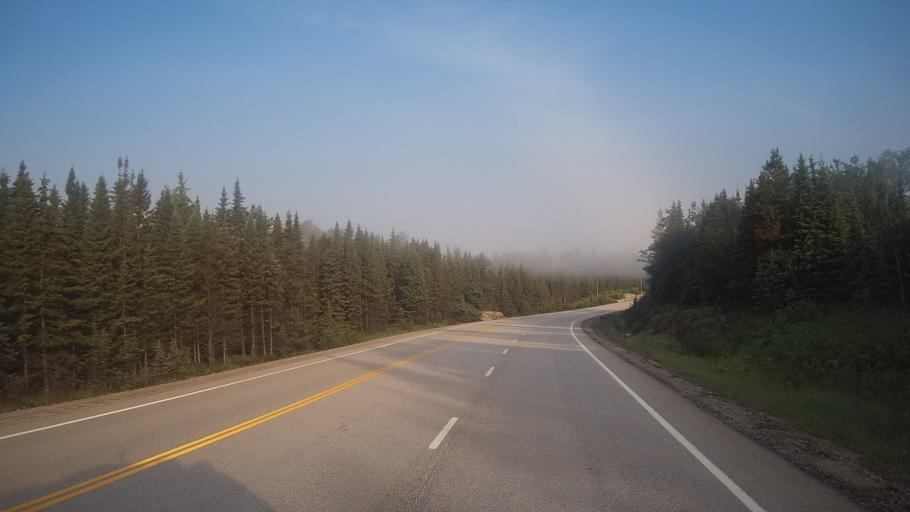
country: CA
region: Ontario
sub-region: Rainy River District
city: Atikokan
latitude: 49.2598
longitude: -91.2091
